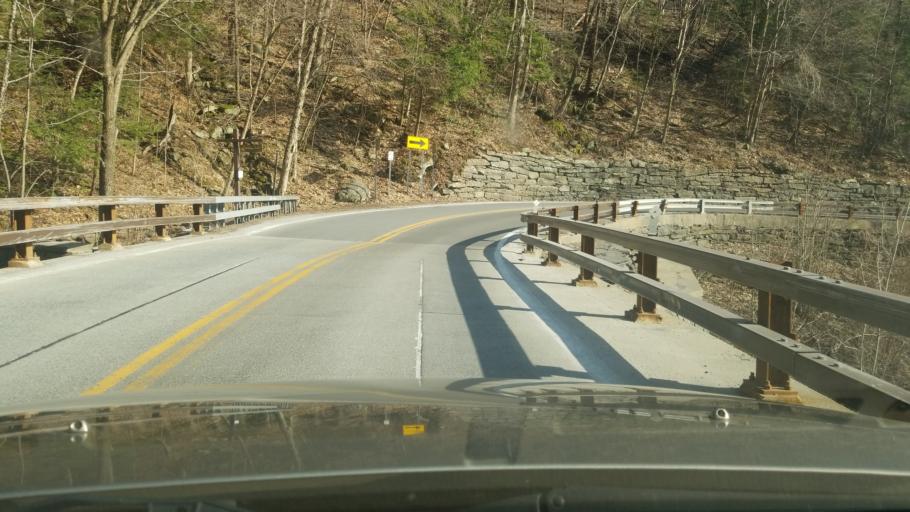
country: US
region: New York
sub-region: Greene County
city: Palenville
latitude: 42.1914
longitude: -74.0707
